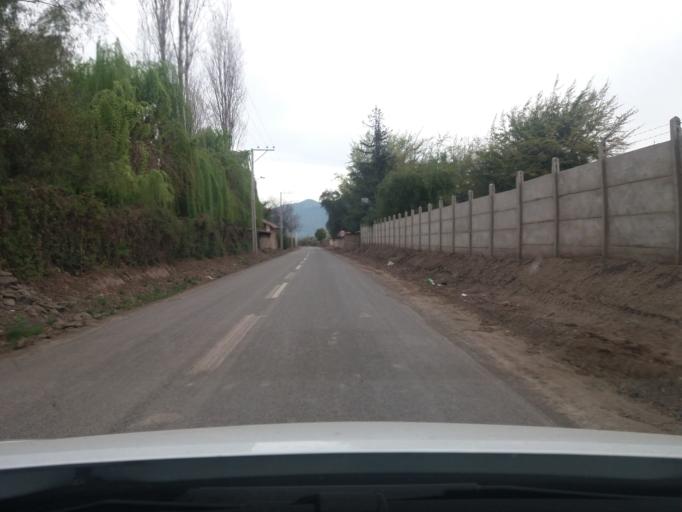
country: CL
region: Valparaiso
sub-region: Provincia de Los Andes
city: Los Andes
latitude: -32.8502
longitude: -70.6330
